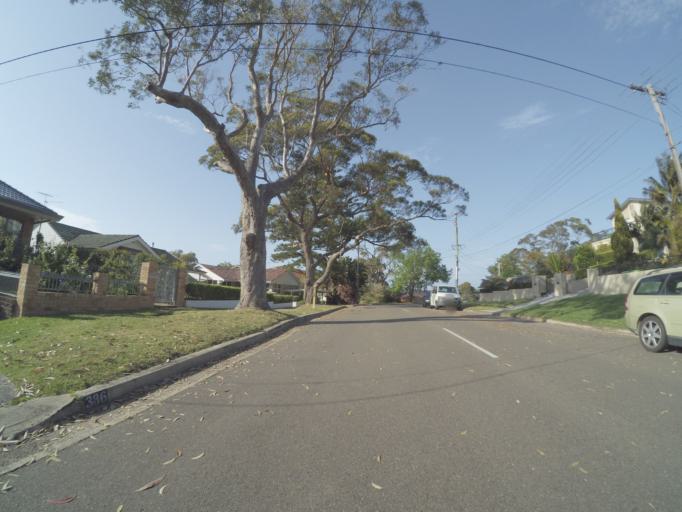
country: AU
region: New South Wales
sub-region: Sutherland Shire
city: Dolans Bay
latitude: -34.0712
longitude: 151.1378
